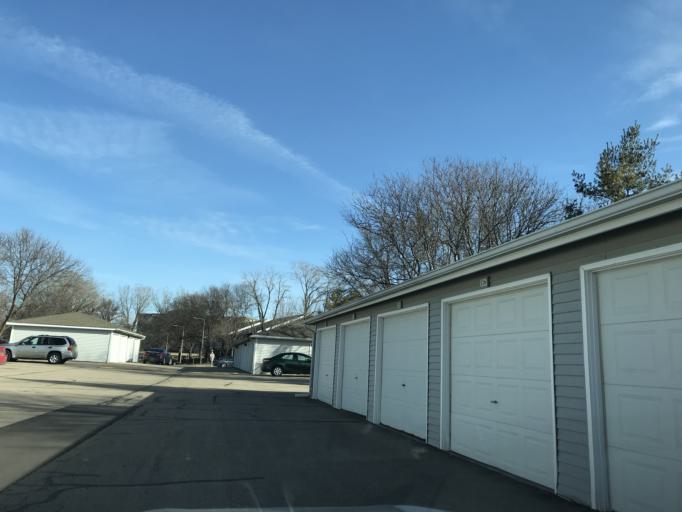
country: US
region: Wisconsin
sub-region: Dane County
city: Maple Bluff
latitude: 43.1417
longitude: -89.3022
